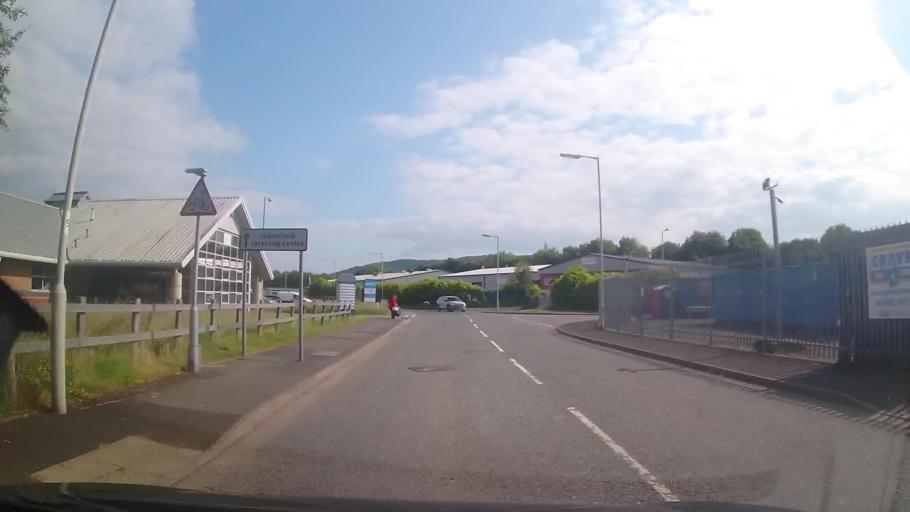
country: GB
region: England
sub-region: Shropshire
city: Craven Arms
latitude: 52.4465
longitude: -2.8420
